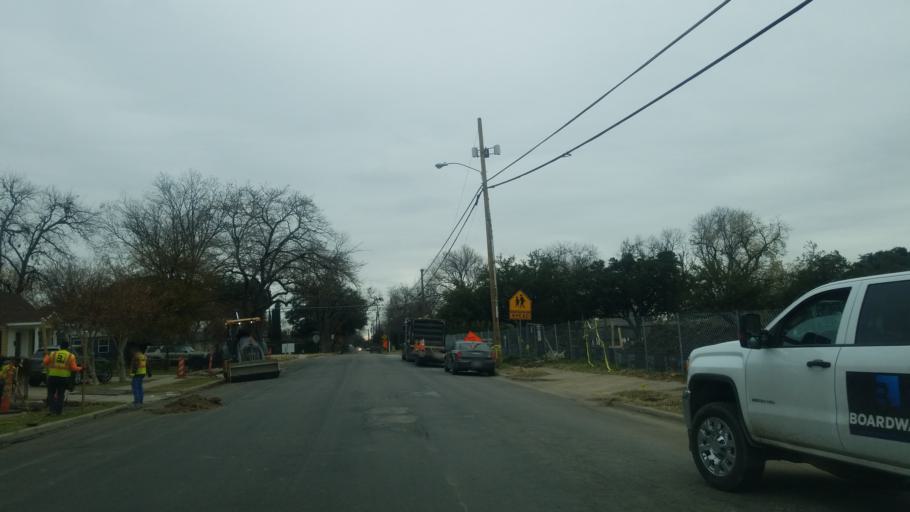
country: US
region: Texas
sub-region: Dallas County
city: Highland Park
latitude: 32.8210
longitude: -96.8310
